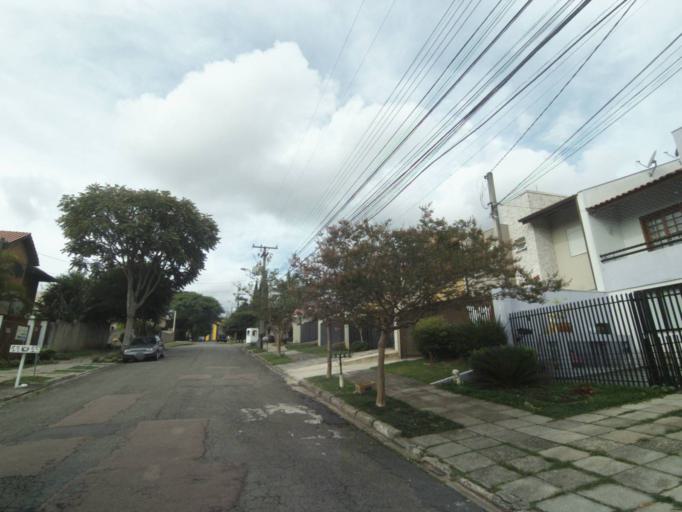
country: BR
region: Parana
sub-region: Curitiba
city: Curitiba
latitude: -25.4443
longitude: -49.3106
